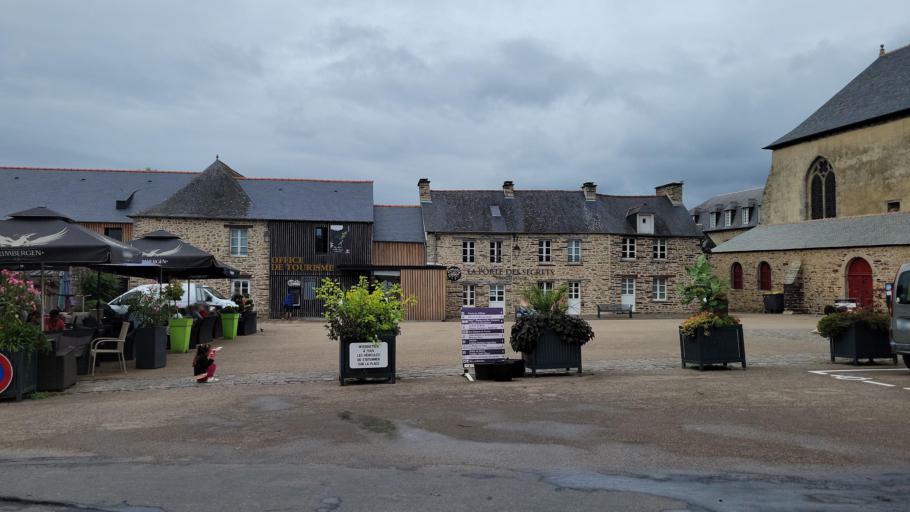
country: FR
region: Brittany
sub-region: Departement d'Ille-et-Vilaine
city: Paimpont
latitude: 48.0189
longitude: -2.1734
